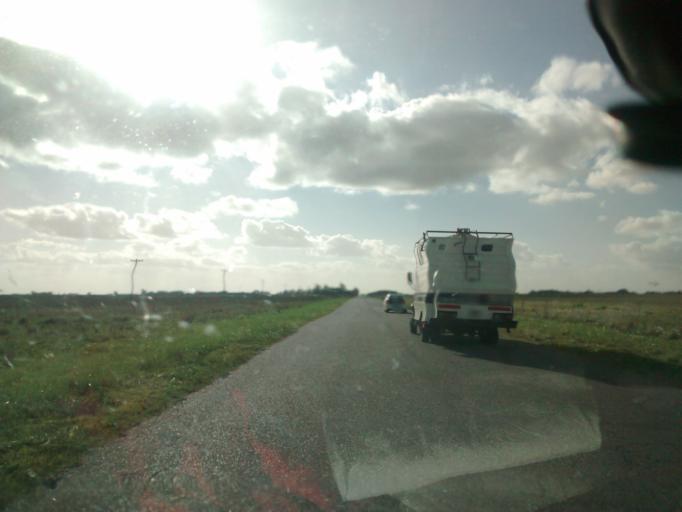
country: AR
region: Buenos Aires
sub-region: Partido de Ayacucho
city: Ayacucho
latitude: -37.1719
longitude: -58.5241
